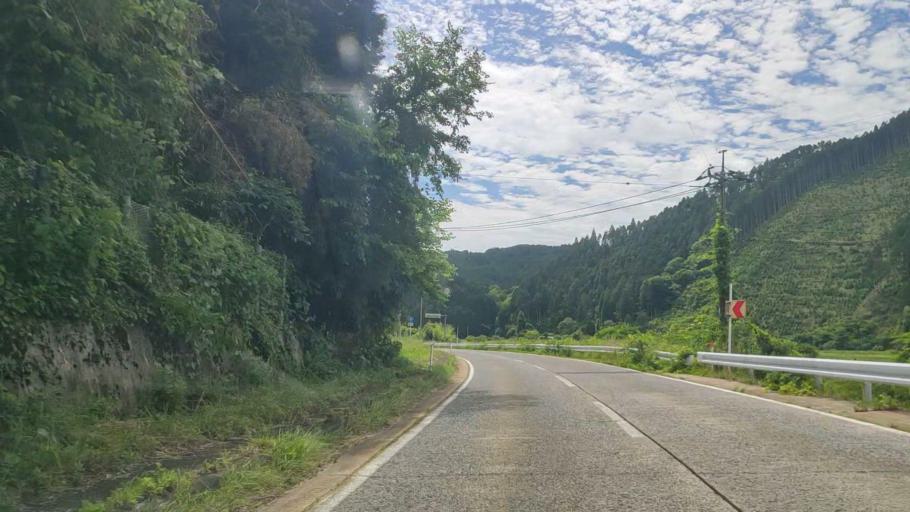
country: JP
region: Okayama
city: Niimi
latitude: 35.1631
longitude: 133.5801
